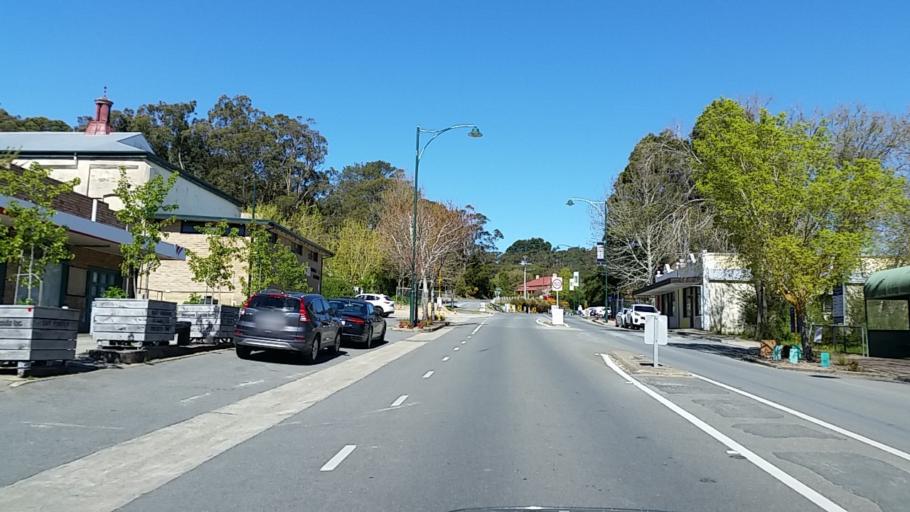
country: AU
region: South Australia
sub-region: Adelaide Hills
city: Bridgewater
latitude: -34.9562
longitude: 138.7446
